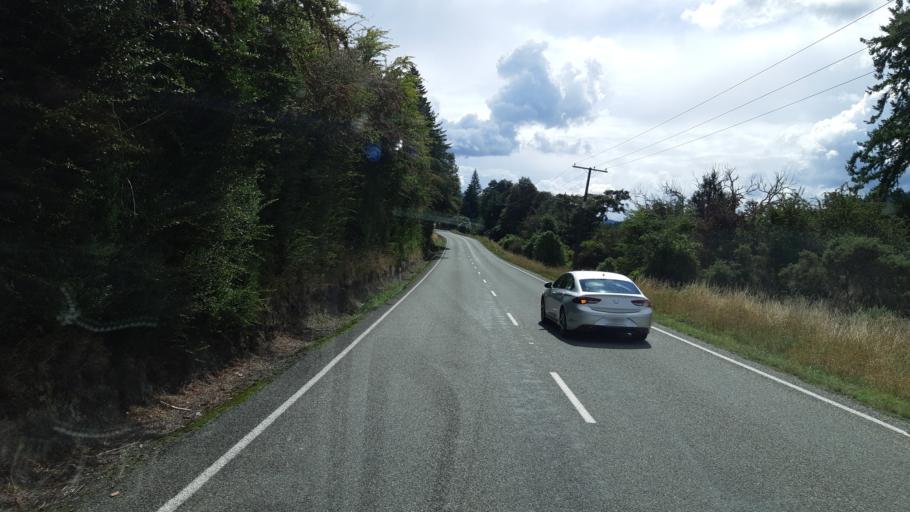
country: NZ
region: Tasman
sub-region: Tasman District
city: Wakefield
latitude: -41.5029
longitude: 172.7949
